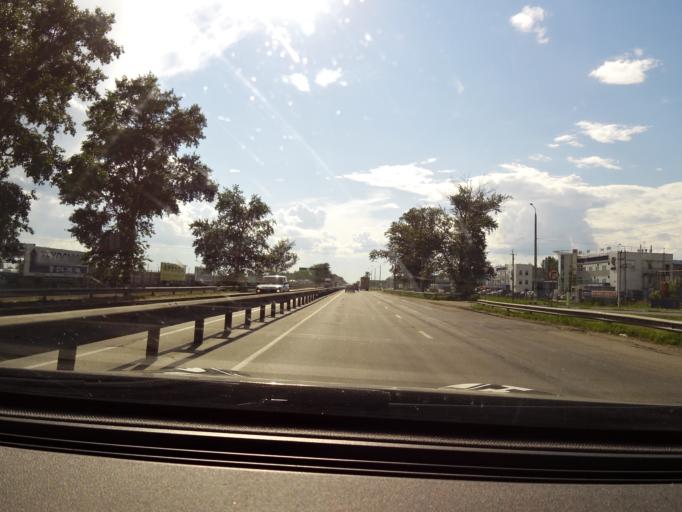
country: RU
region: Nizjnij Novgorod
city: Gorbatovka
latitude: 56.3108
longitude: 43.7975
